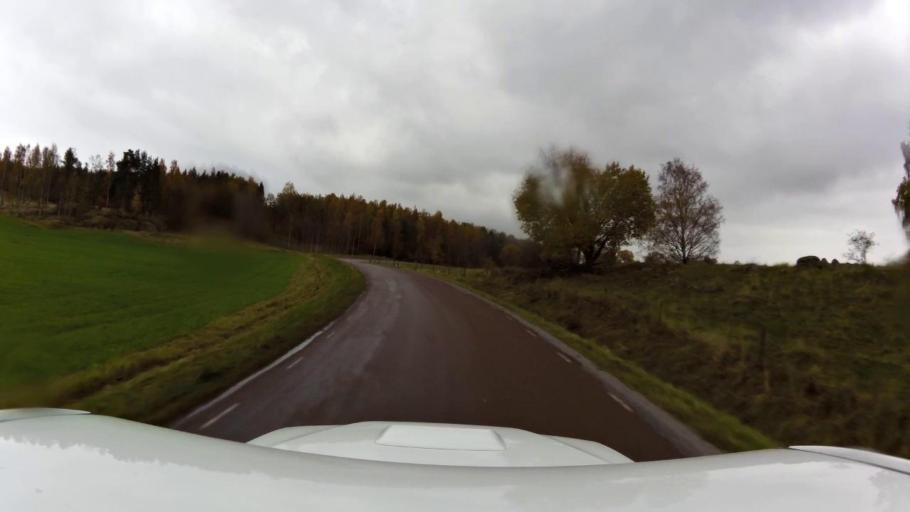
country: SE
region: OEstergoetland
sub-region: Linkopings Kommun
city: Ljungsbro
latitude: 58.5314
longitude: 15.5236
